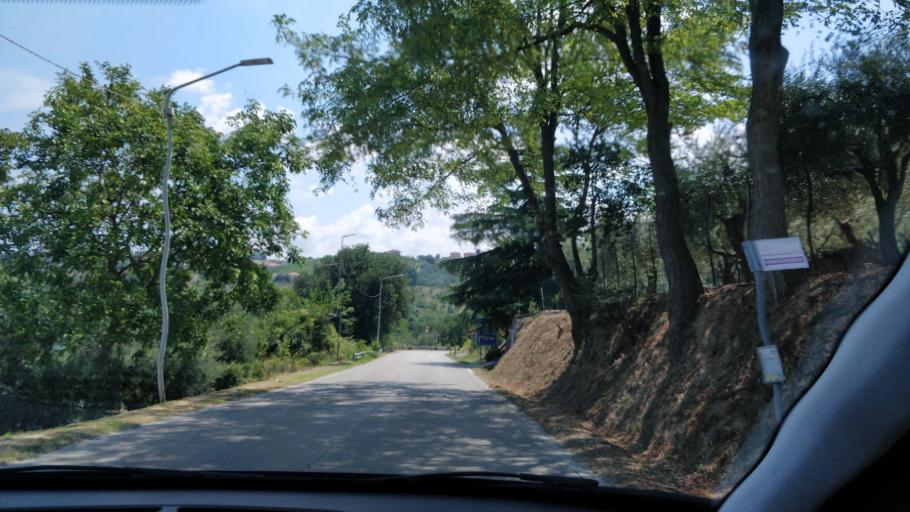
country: IT
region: Abruzzo
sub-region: Provincia di Chieti
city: Sambuceto
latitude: 42.4058
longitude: 14.1977
